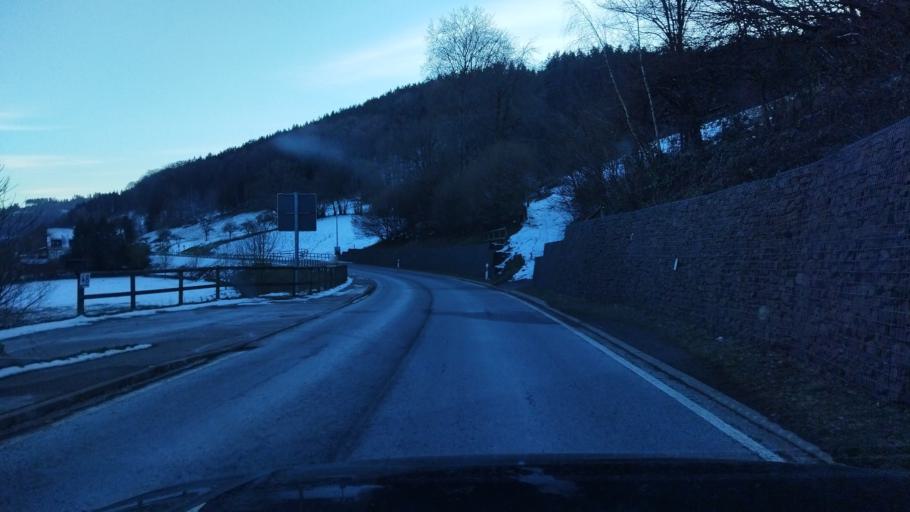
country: DE
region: Hesse
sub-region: Regierungsbezirk Darmstadt
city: Beerfelden
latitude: 49.5489
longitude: 9.0110
